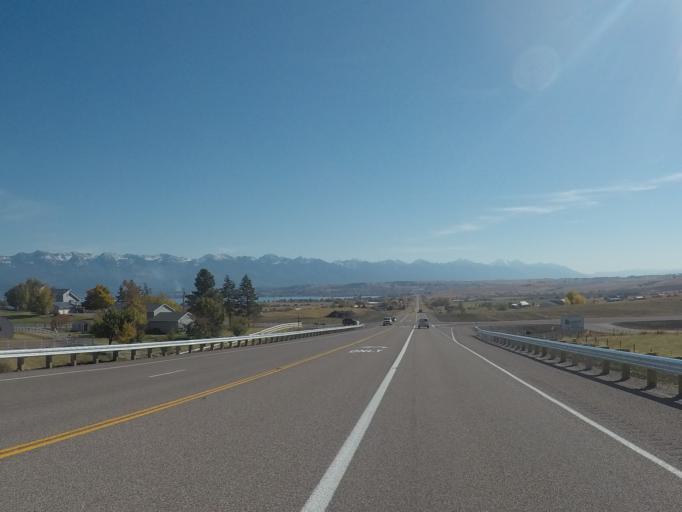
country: US
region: Montana
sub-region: Lake County
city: Polson
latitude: 47.7339
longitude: -114.2185
